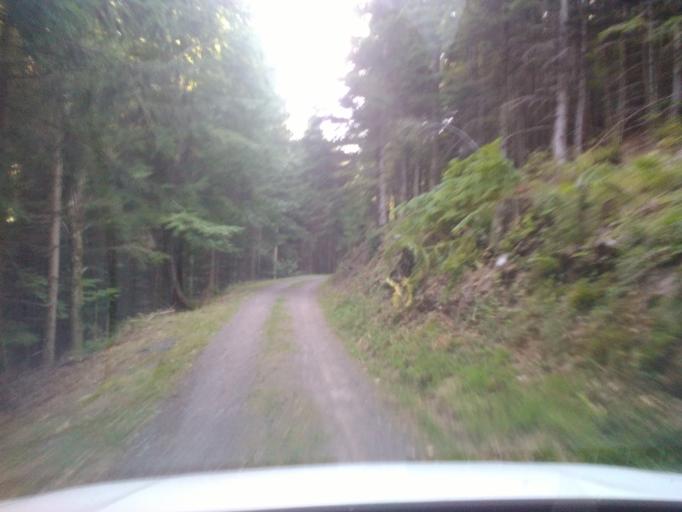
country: FR
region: Lorraine
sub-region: Departement des Vosges
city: Senones
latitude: 48.4332
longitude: 7.0346
